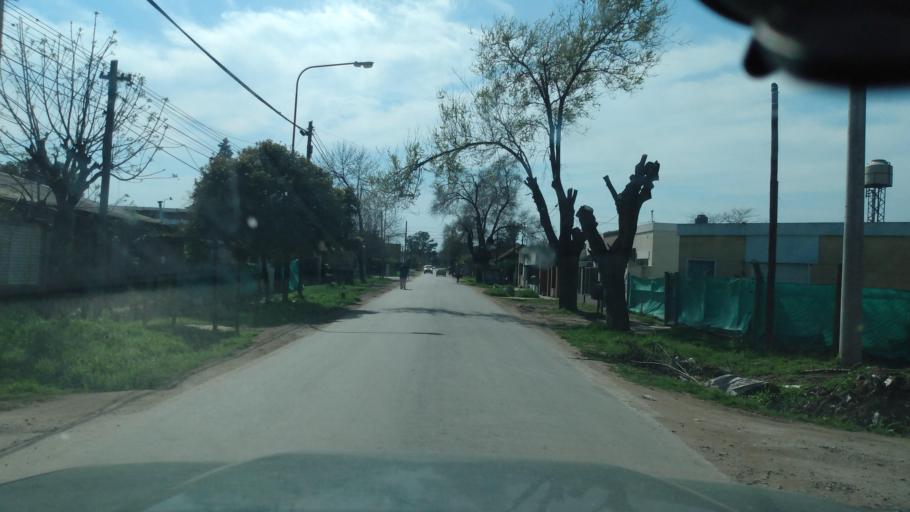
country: AR
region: Buenos Aires
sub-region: Partido de Lujan
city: Lujan
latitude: -34.5509
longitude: -59.1054
